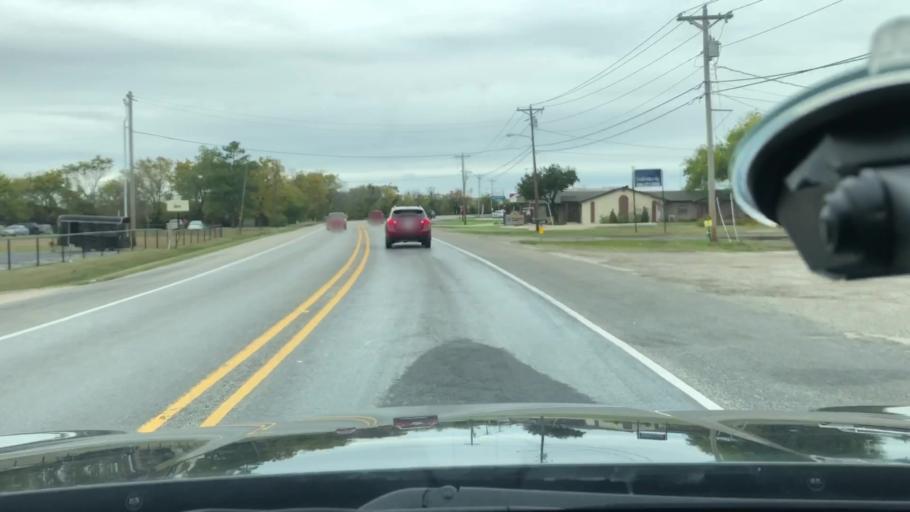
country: US
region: Texas
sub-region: Hunt County
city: Greenville
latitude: 33.0870
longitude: -96.1088
